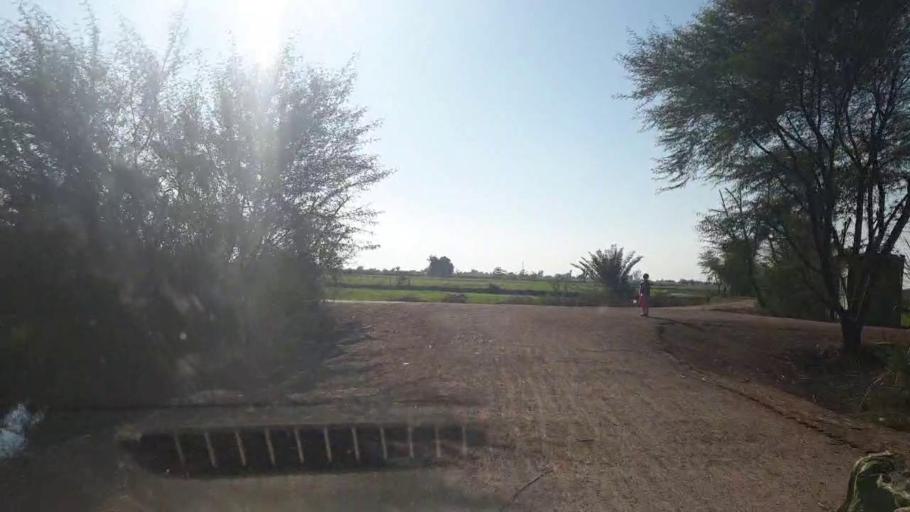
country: PK
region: Sindh
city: Shahdadpur
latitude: 25.9156
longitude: 68.5330
